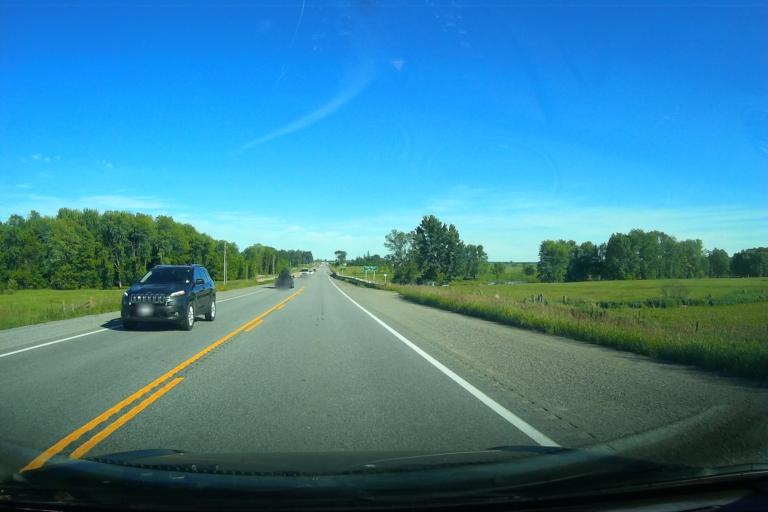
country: CA
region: Ontario
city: Pembroke
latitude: 45.6936
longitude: -76.9571
